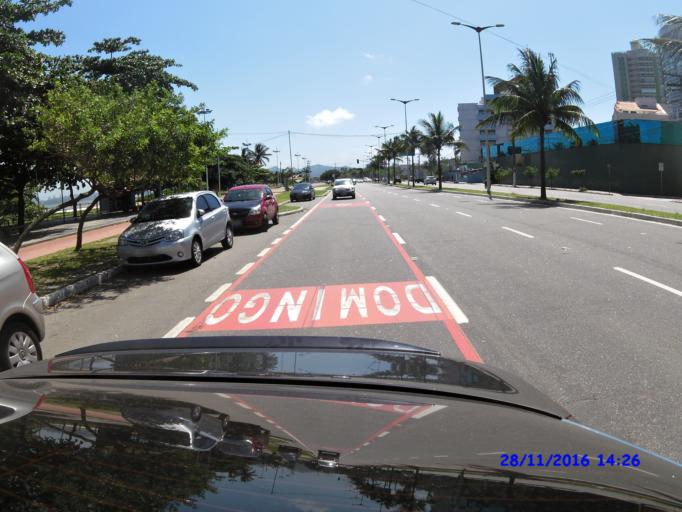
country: BR
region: Espirito Santo
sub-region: Vila Velha
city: Vila Velha
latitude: -20.2662
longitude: -40.2678
